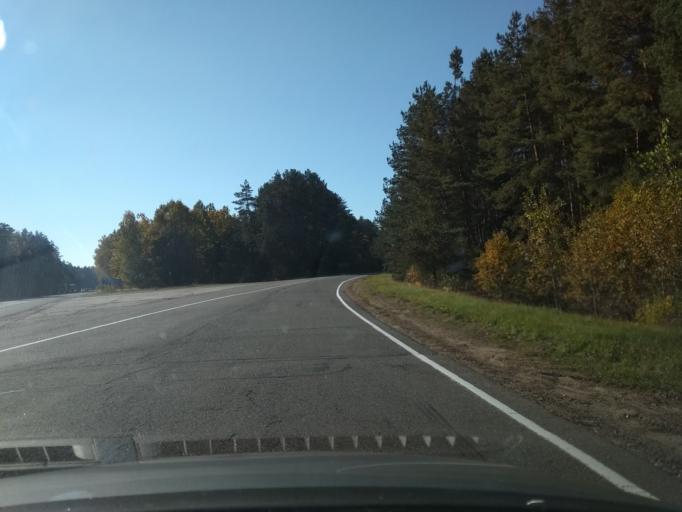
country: BY
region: Brest
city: Baranovichi
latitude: 53.0534
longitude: 25.8595
